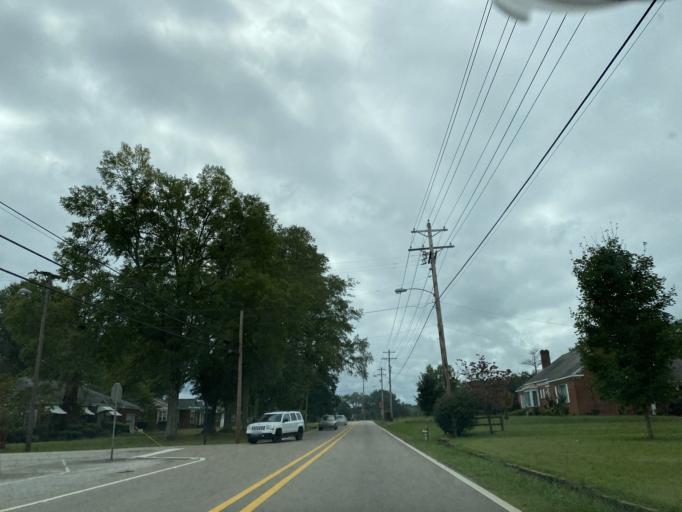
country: US
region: Mississippi
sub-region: Tishomingo County
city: Belmont
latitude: 34.5056
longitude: -88.2071
